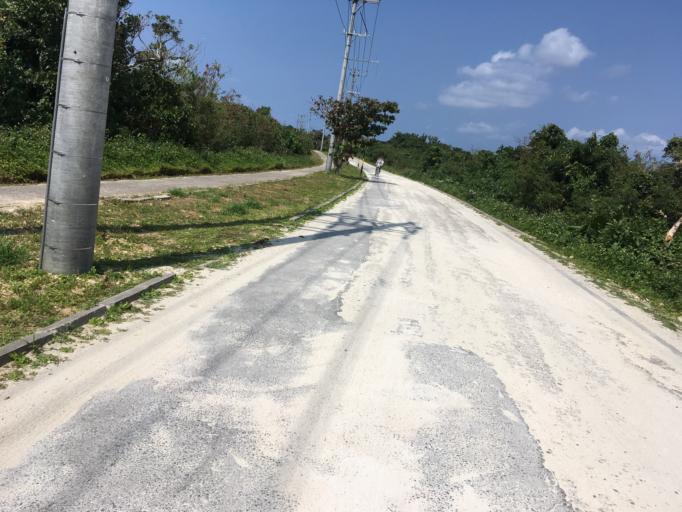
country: JP
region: Okinawa
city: Ishigaki
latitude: 24.3291
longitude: 124.0803
